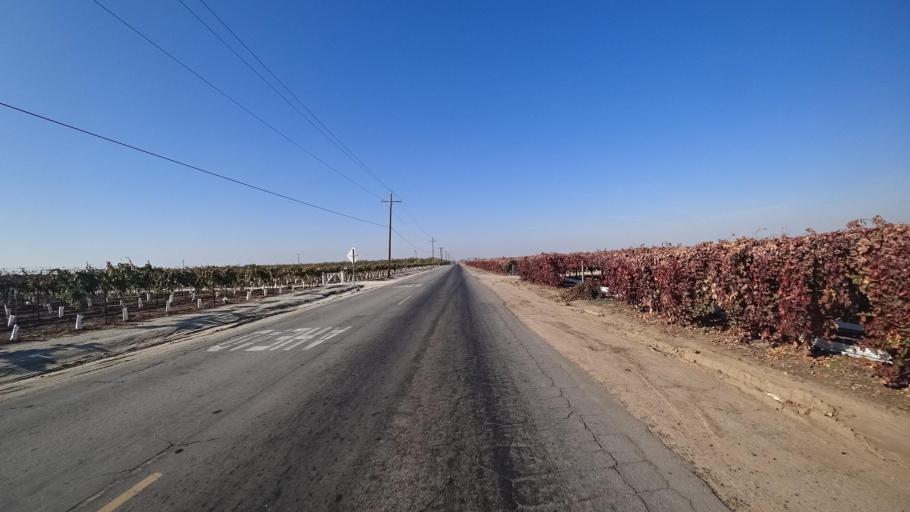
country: US
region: California
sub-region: Kern County
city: McFarland
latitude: 35.7178
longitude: -119.2068
